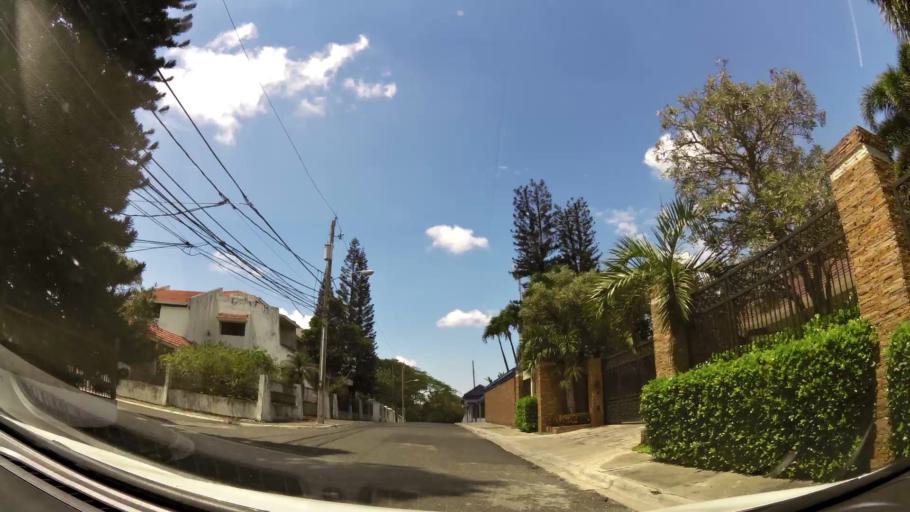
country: DO
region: Santiago
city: Santiago de los Caballeros
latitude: 19.4668
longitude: -70.6807
